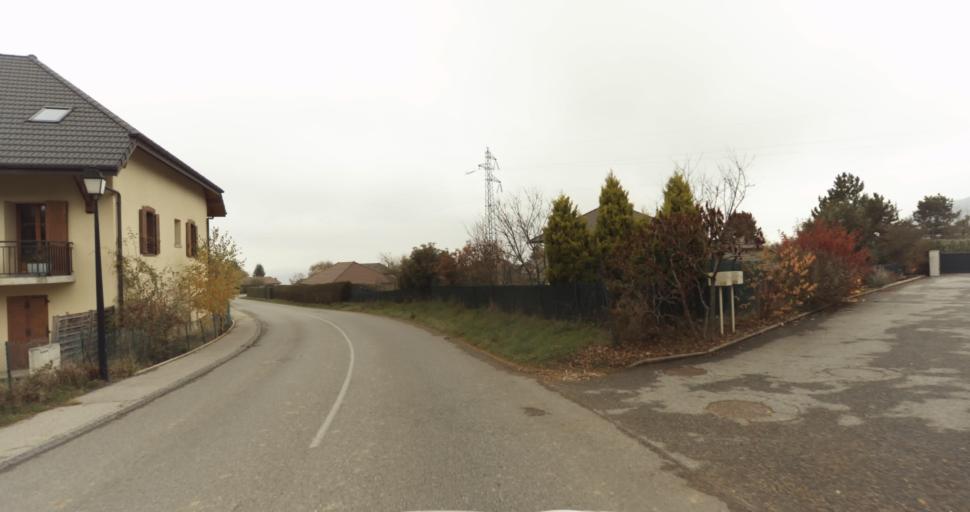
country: FR
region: Rhone-Alpes
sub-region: Departement de la Haute-Savoie
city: Viuz-la-Chiesaz
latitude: 45.8427
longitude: 6.0849
